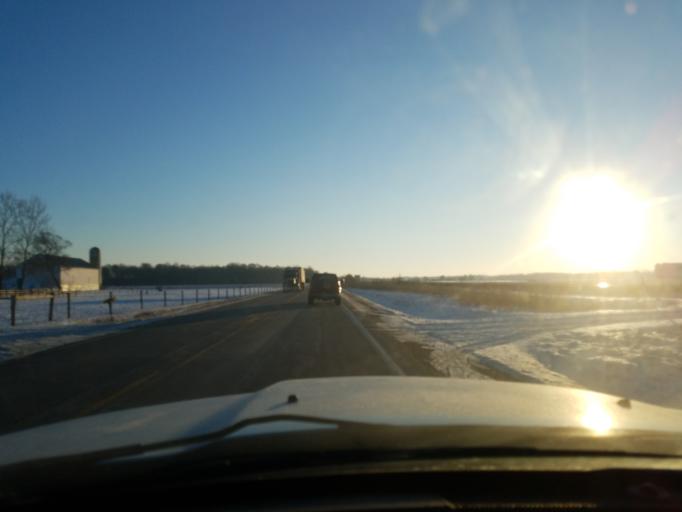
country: US
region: Indiana
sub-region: Elkhart County
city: Nappanee
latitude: 41.4460
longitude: -86.0668
